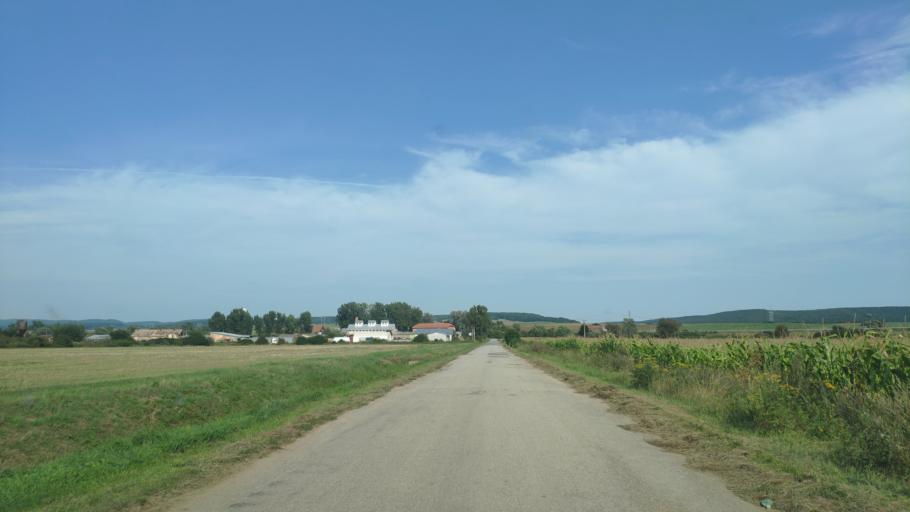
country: HU
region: Borsod-Abauj-Zemplen
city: Putnok
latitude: 48.4543
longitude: 20.3368
